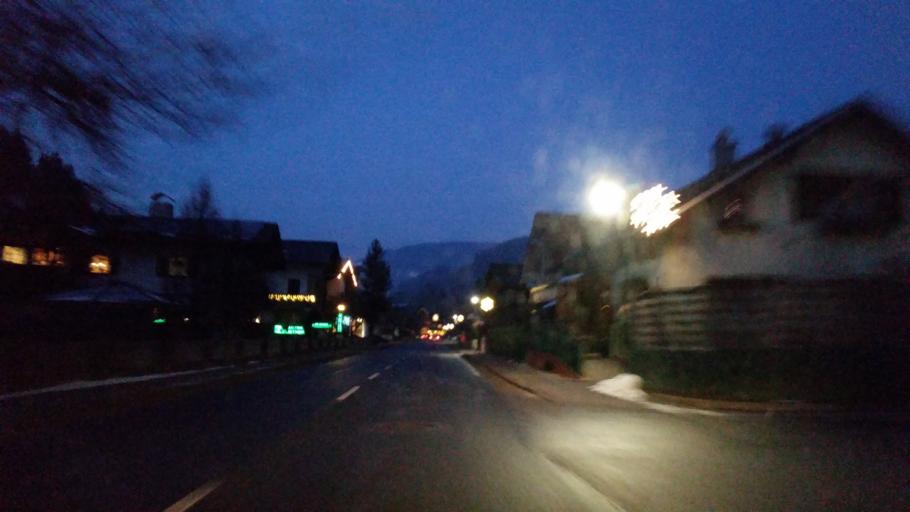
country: AT
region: Salzburg
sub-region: Politischer Bezirk Hallein
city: Abtenau
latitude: 47.5155
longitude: 13.4313
